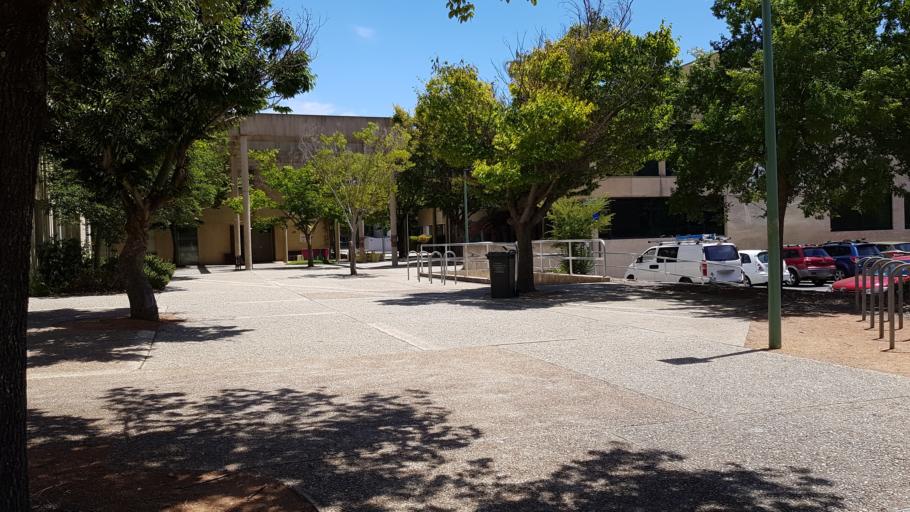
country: AU
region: Australian Capital Territory
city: Forrest
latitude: -35.3448
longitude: 149.0849
